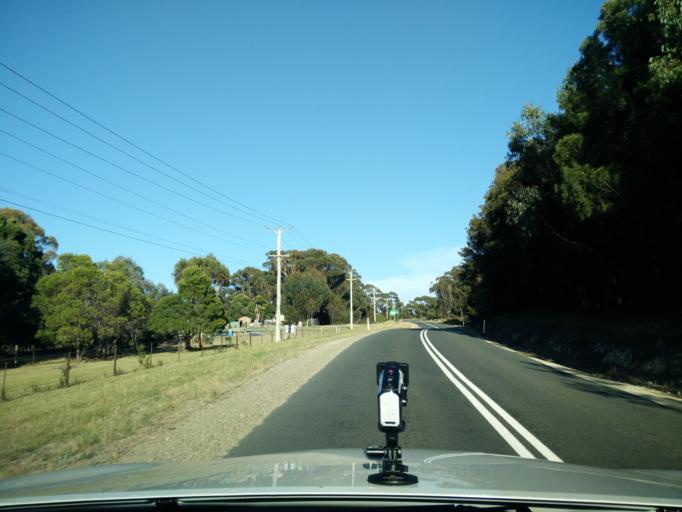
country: AU
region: Tasmania
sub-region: Break O'Day
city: St Helens
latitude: -41.3086
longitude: 148.2222
